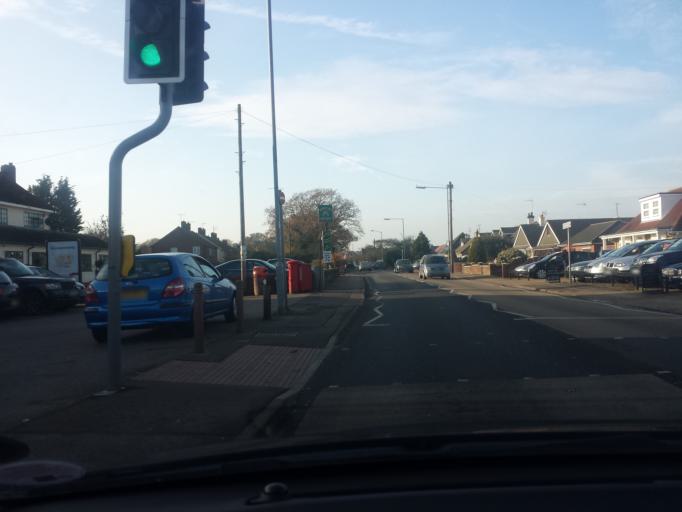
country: GB
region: England
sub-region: Essex
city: Little Clacton
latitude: 51.8040
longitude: 1.1302
